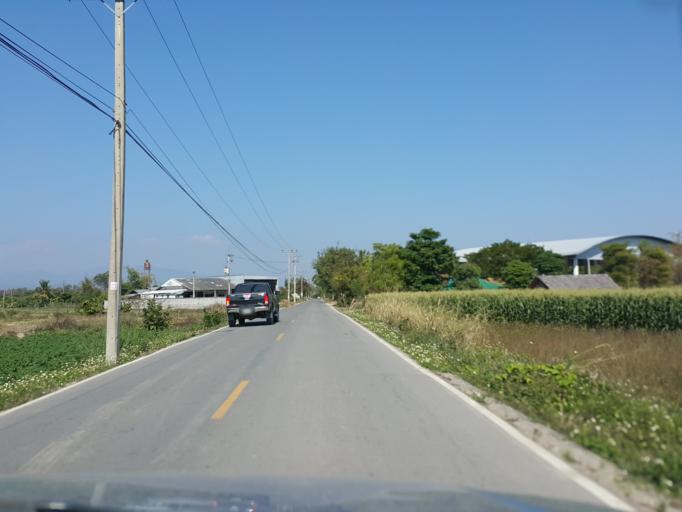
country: TH
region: Chiang Mai
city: Mae Wang
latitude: 18.5933
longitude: 98.7981
